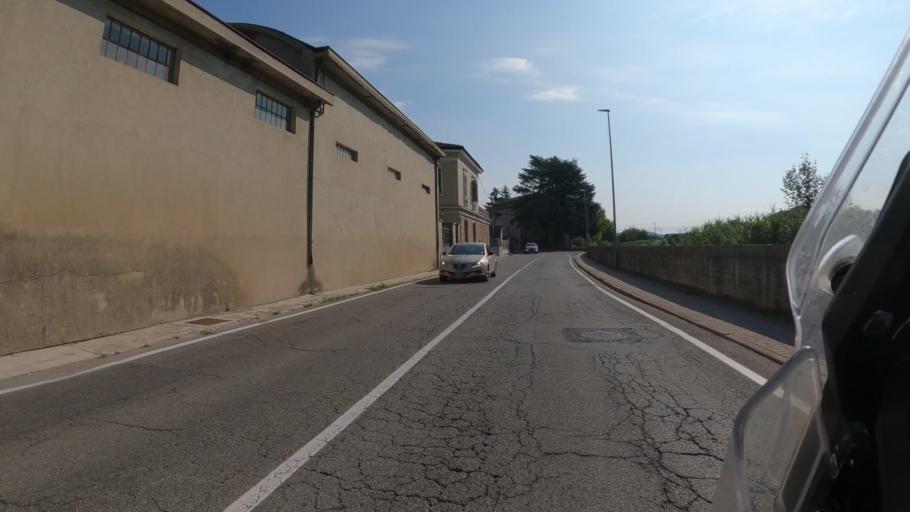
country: IT
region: Piedmont
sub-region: Provincia di Asti
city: Nizza Monferrato
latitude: 44.7757
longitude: 8.3616
